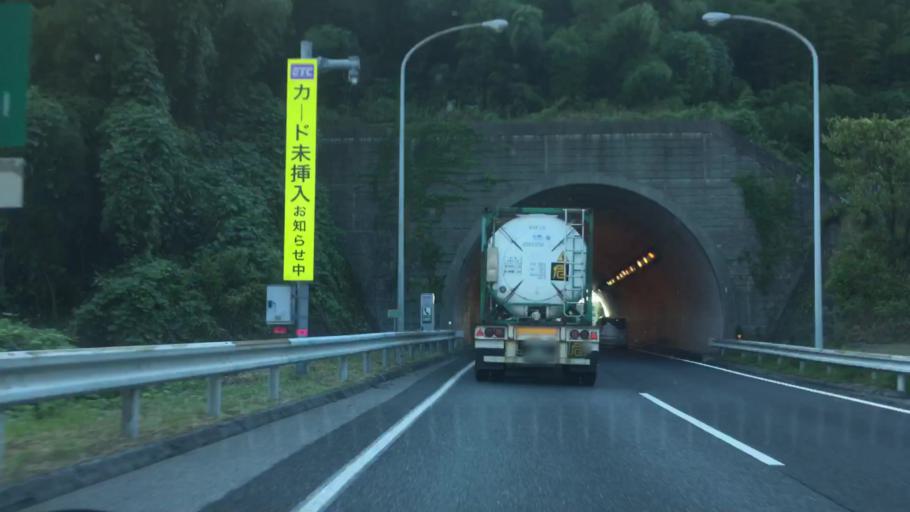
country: JP
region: Yamaguchi
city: Kudamatsu
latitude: 34.0440
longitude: 131.8628
